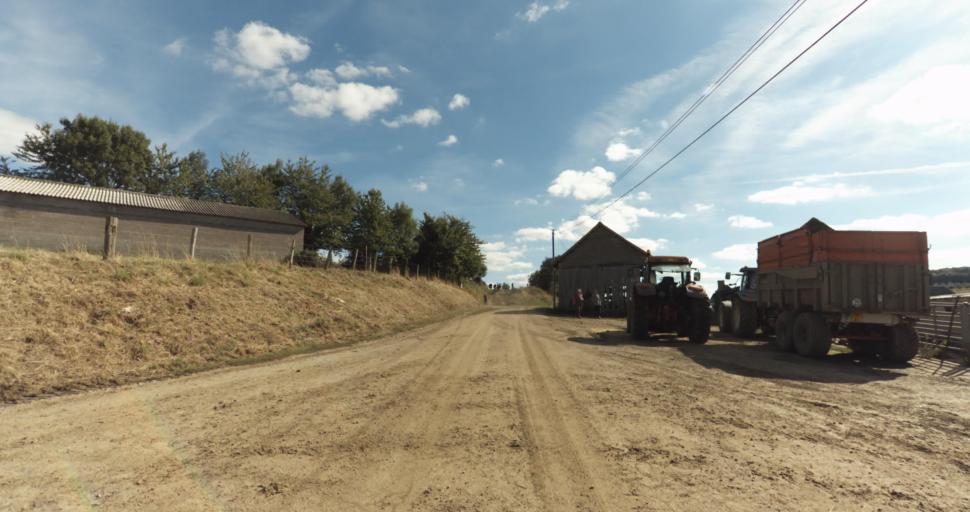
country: FR
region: Lower Normandy
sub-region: Departement de l'Orne
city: Vimoutiers
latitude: 48.9313
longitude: 0.1308
